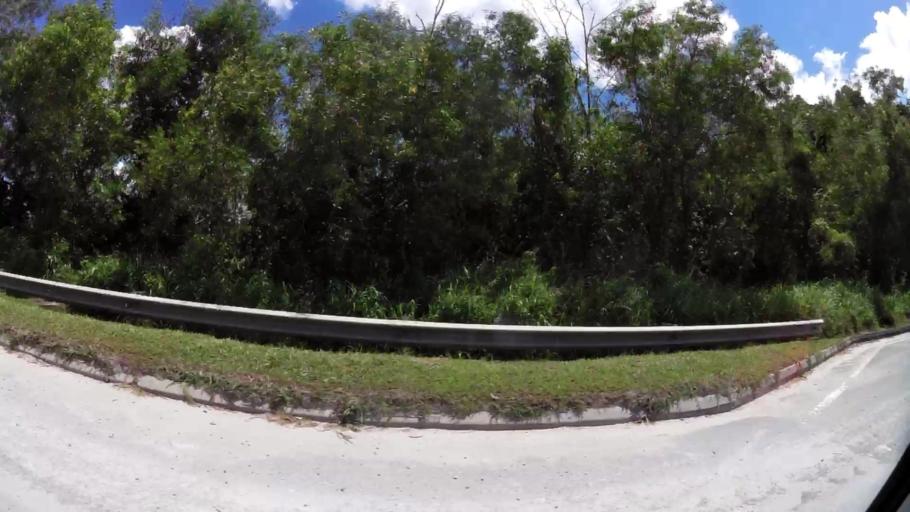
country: BN
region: Brunei and Muara
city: Bandar Seri Begawan
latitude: 4.9338
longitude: 114.9729
